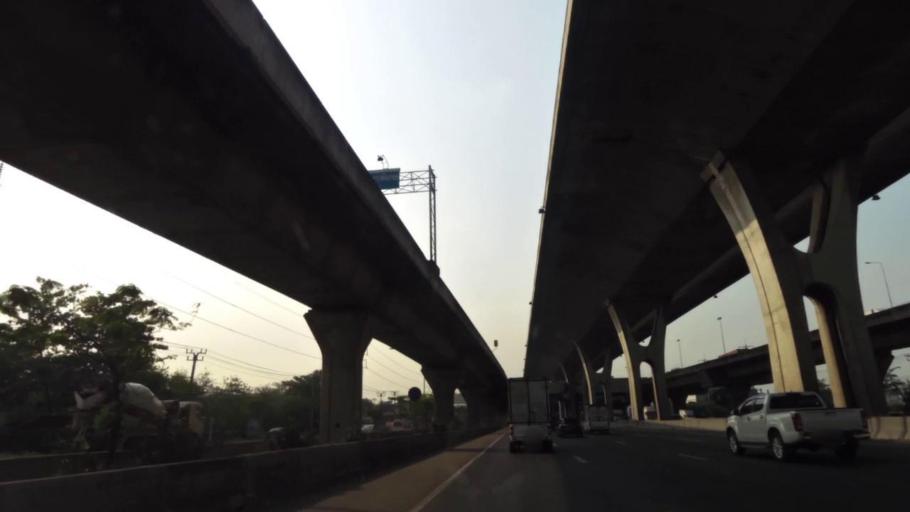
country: TH
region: Bangkok
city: Bang Na
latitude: 13.6386
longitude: 100.7023
